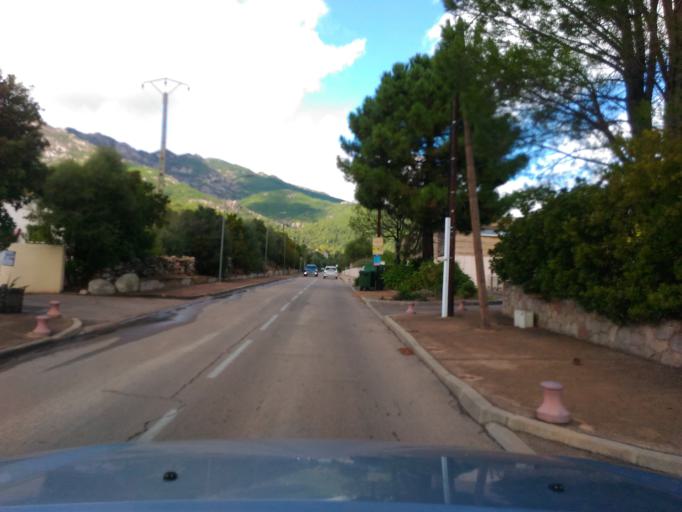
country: FR
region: Corsica
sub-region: Departement de la Corse-du-Sud
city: Porto-Vecchio
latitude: 41.7071
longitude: 9.3177
